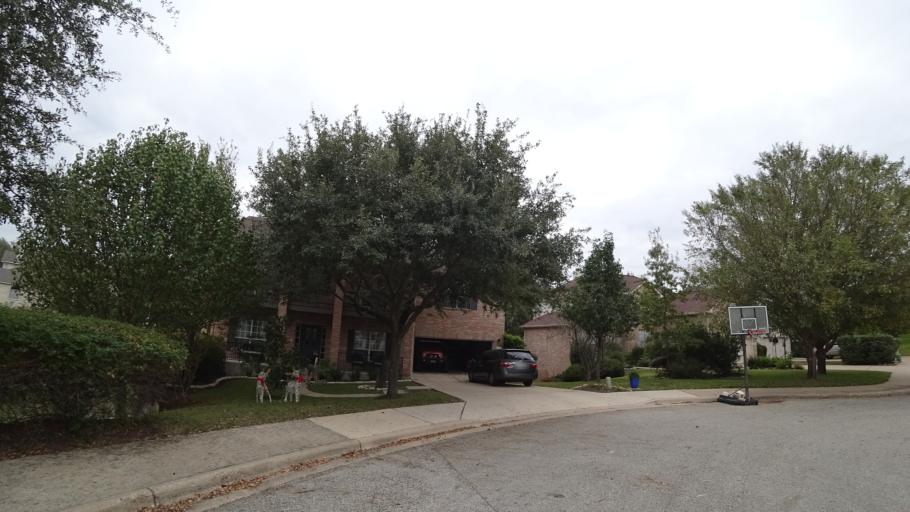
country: US
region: Texas
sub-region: Travis County
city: Bee Cave
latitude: 30.3102
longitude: -97.9295
